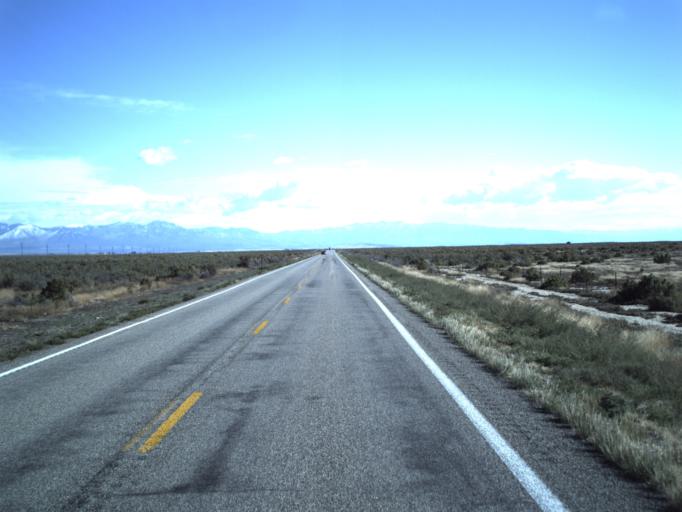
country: US
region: Utah
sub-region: Millard County
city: Delta
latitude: 39.2844
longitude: -112.4624
